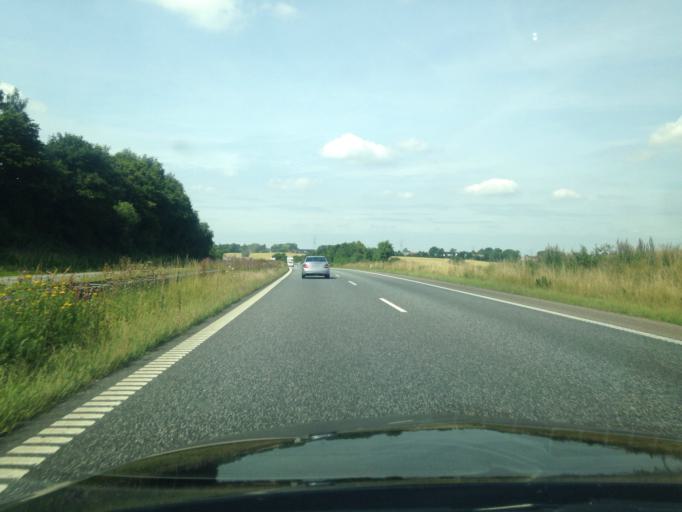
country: DK
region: South Denmark
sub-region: Fredericia Kommune
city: Taulov
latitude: 55.5452
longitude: 9.5805
